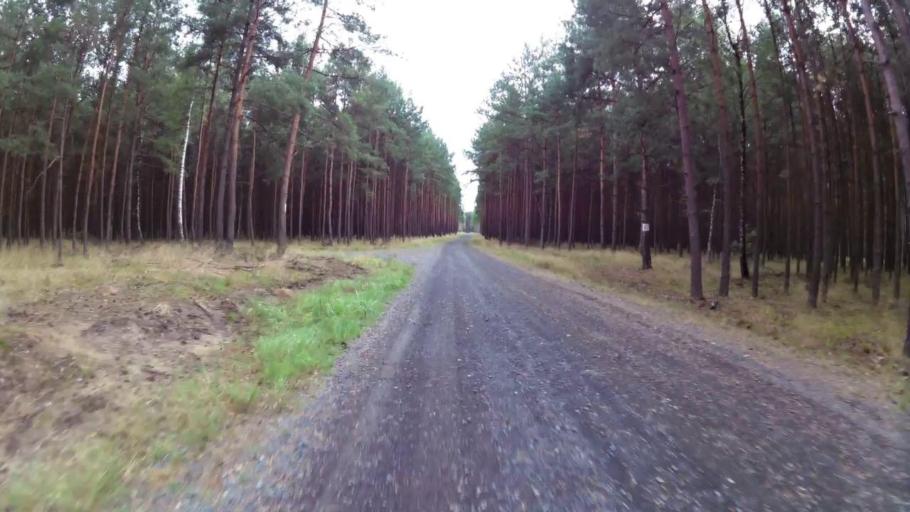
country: PL
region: West Pomeranian Voivodeship
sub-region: Powiat mysliborski
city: Debno
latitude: 52.7858
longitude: 14.7213
